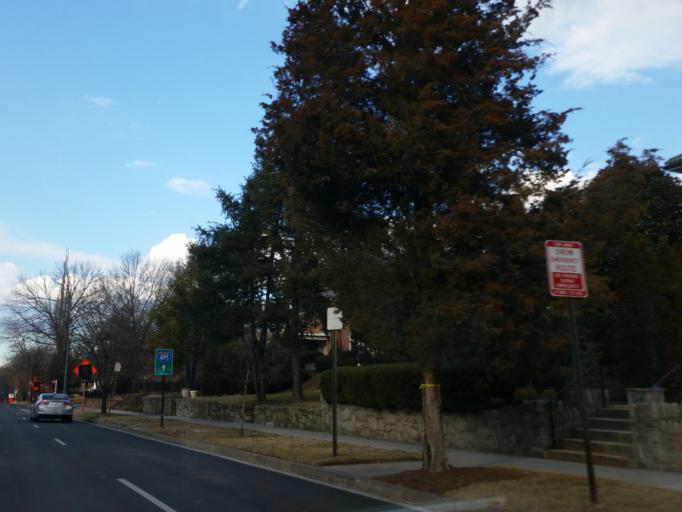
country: US
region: Maryland
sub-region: Montgomery County
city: Silver Spring
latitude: 38.9593
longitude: -77.0363
